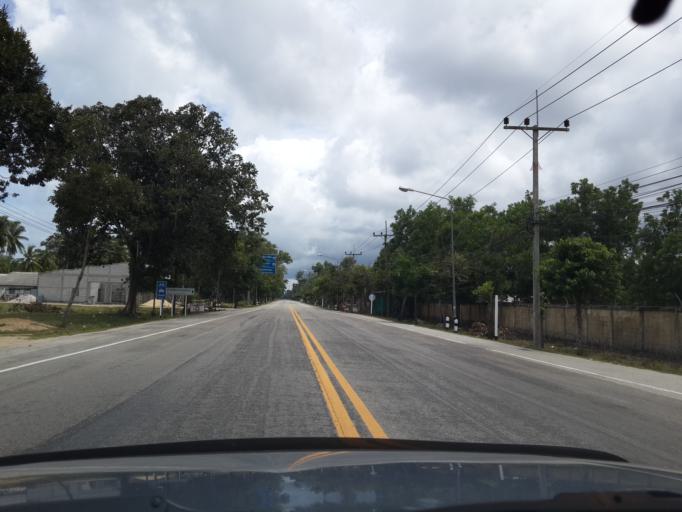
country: TH
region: Narathiwat
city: Bacho
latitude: 6.5214
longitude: 101.7513
